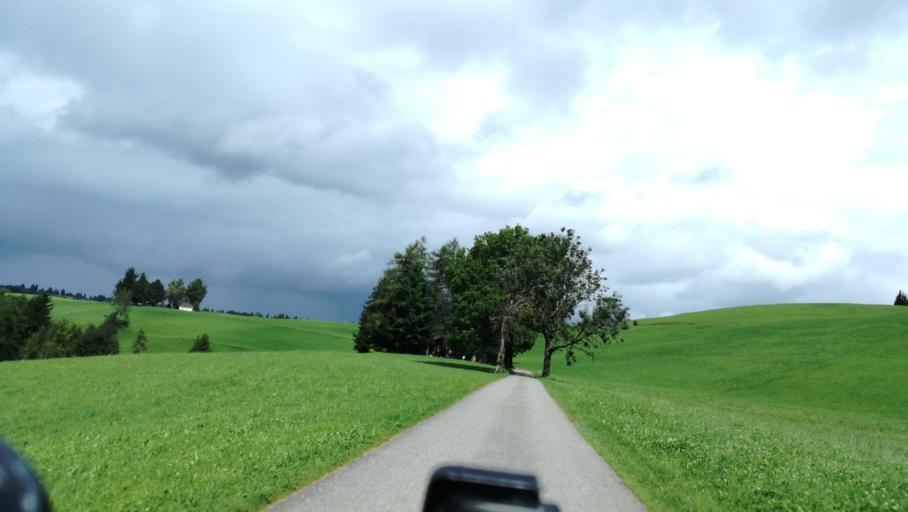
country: CH
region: Zug
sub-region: Zug
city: Walchwil
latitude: 47.1084
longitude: 8.5462
